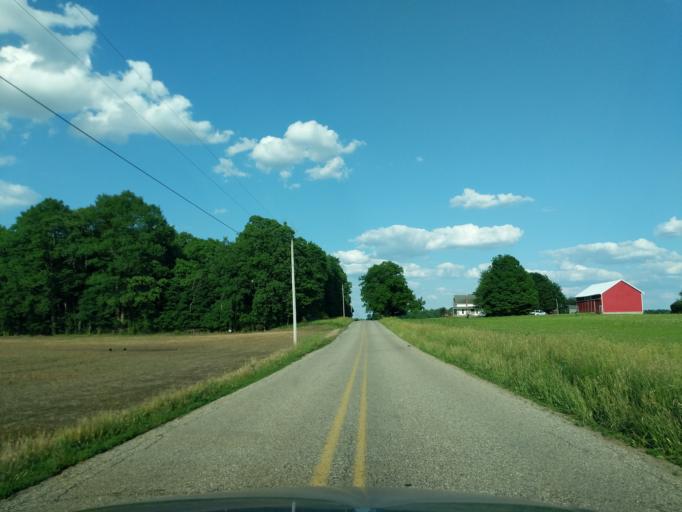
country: US
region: Indiana
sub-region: Kosciusko County
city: North Webster
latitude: 41.3024
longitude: -85.6232
